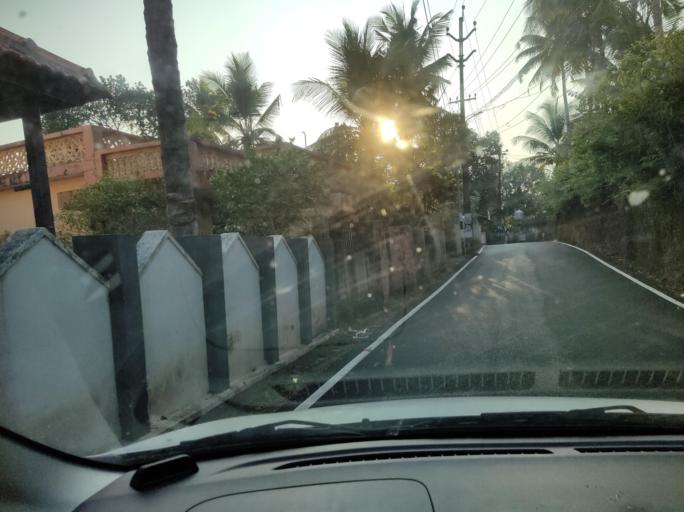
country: IN
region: Kerala
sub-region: Pattanamtitta
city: Tiruvalla
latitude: 9.3698
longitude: 76.5724
